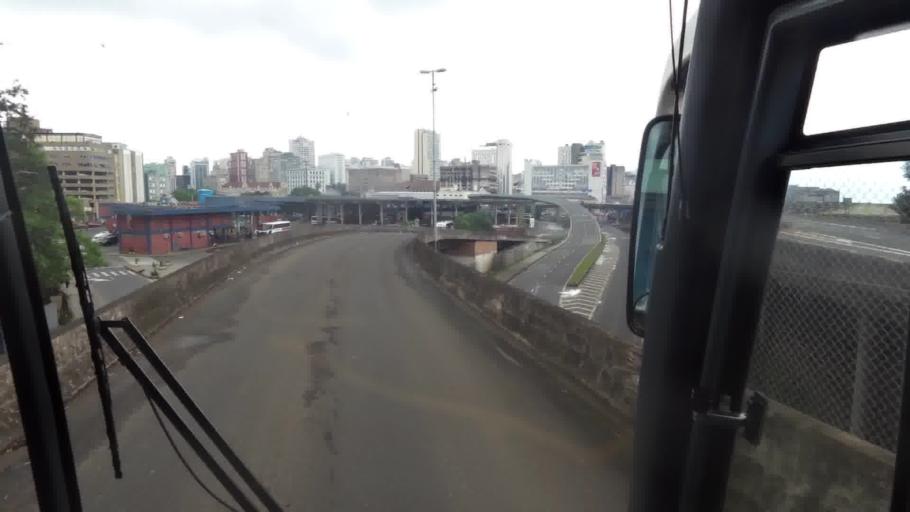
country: BR
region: Rio Grande do Sul
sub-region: Porto Alegre
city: Porto Alegre
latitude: -30.0213
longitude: -51.2181
